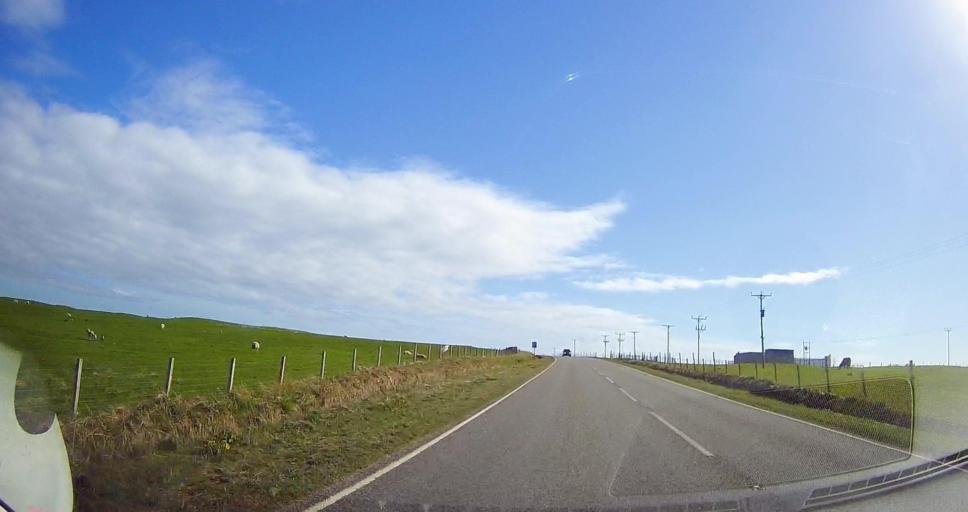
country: GB
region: Scotland
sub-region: Shetland Islands
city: Sandwick
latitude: 59.9000
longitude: -1.3034
